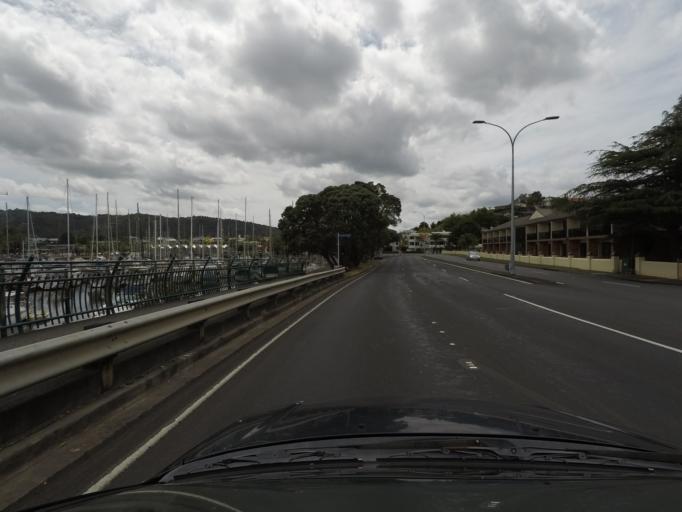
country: NZ
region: Northland
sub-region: Whangarei
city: Whangarei
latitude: -35.7242
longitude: 174.3276
